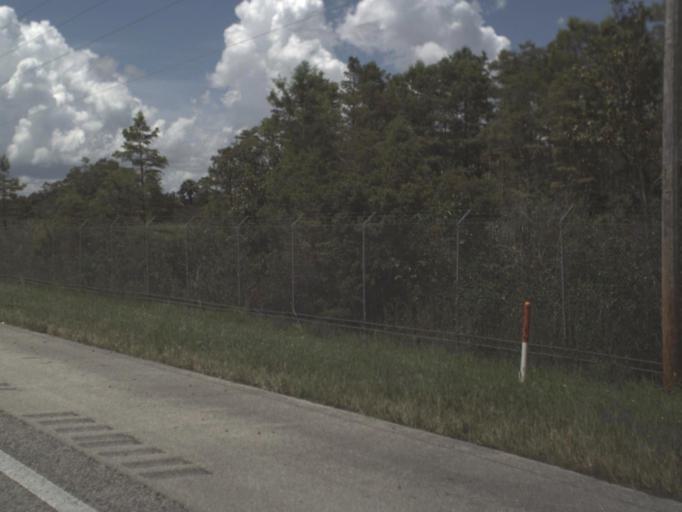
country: US
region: Florida
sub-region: Collier County
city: Immokalee
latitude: 26.1674
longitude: -81.1830
